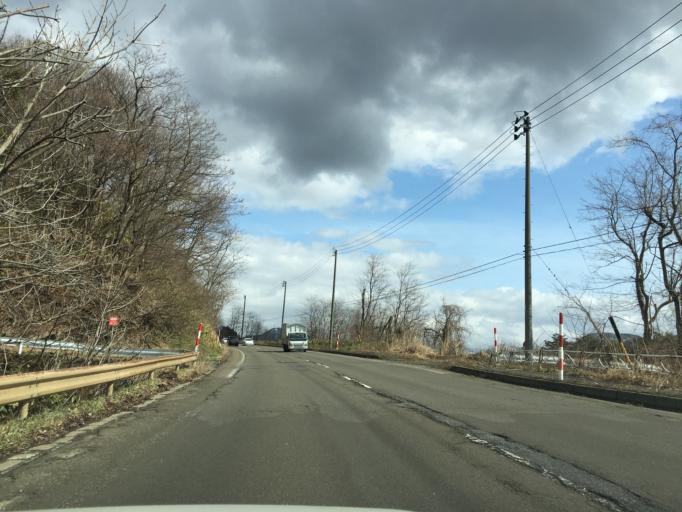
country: JP
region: Akita
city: Odate
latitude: 40.2168
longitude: 140.6334
